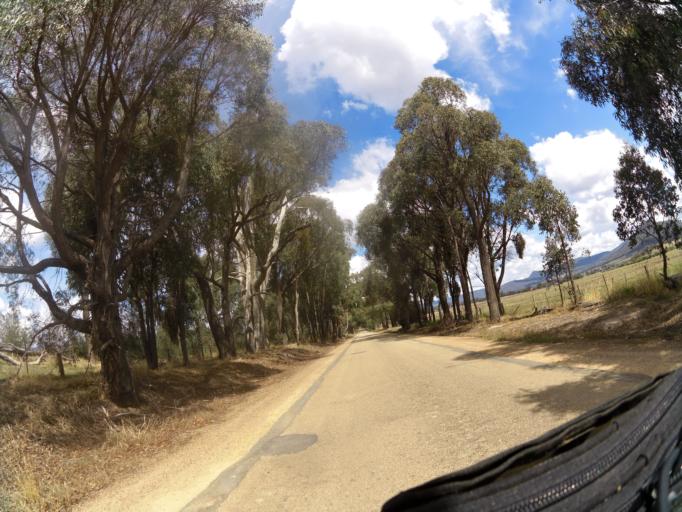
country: AU
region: Victoria
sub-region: Benalla
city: Benalla
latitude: -36.7671
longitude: 145.9759
